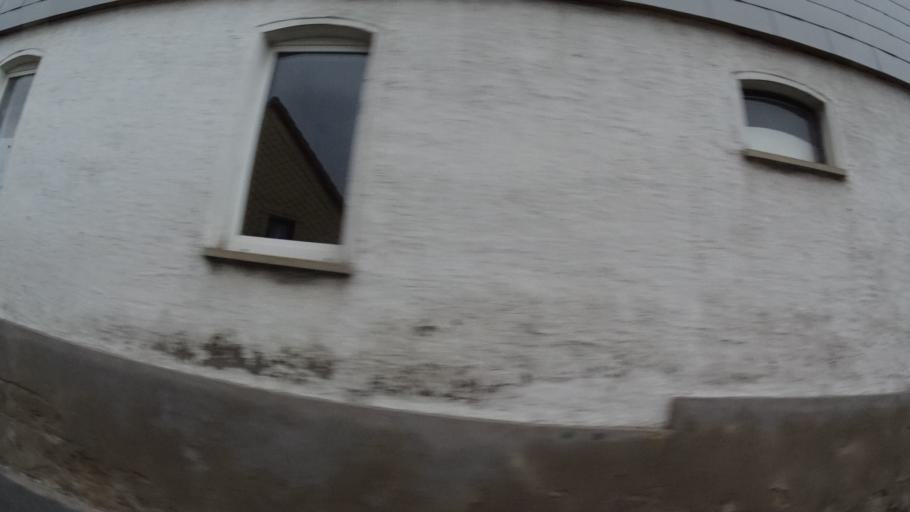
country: DE
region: Thuringia
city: Possneck
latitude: 50.6981
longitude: 11.6040
